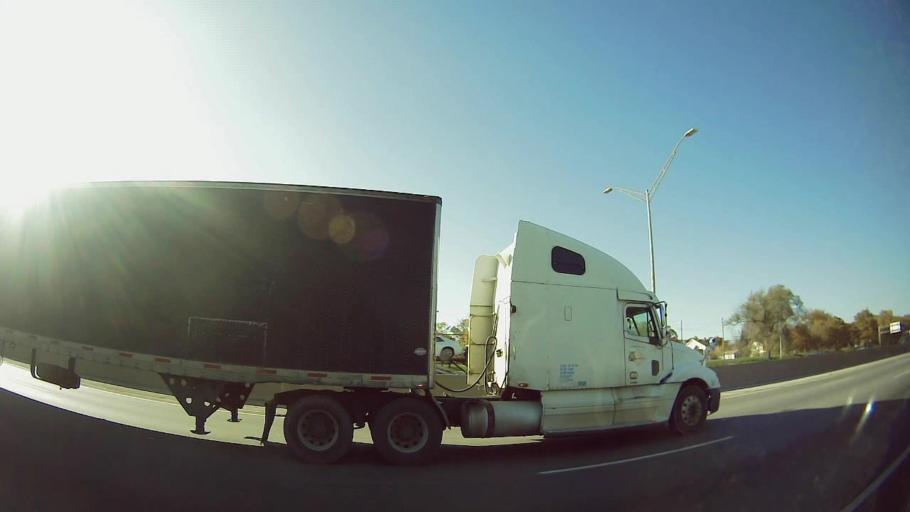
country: US
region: Michigan
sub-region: Oakland County
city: Hazel Park
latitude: 42.4350
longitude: -83.0947
